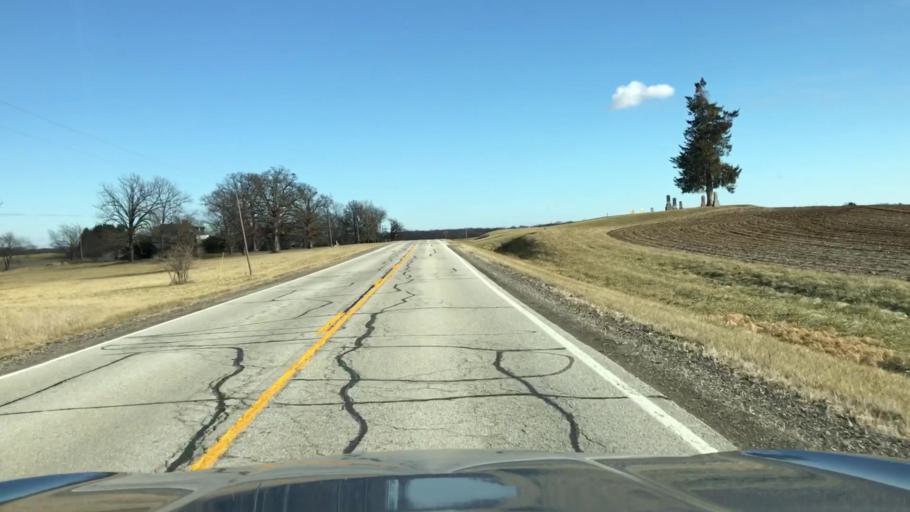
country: US
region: Illinois
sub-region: McLean County
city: Gridley
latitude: 40.6564
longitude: -88.9052
